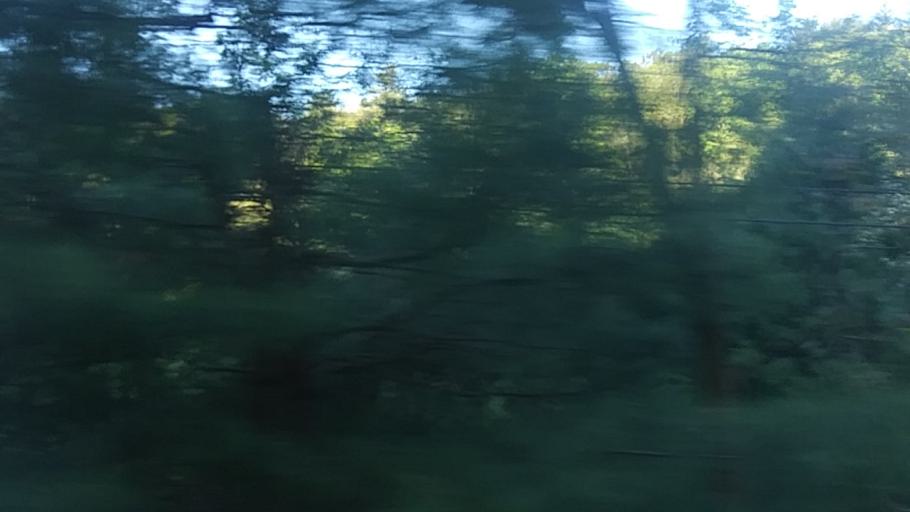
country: US
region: Massachusetts
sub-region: Franklin County
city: Buckland
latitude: 42.5747
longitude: -72.7731
